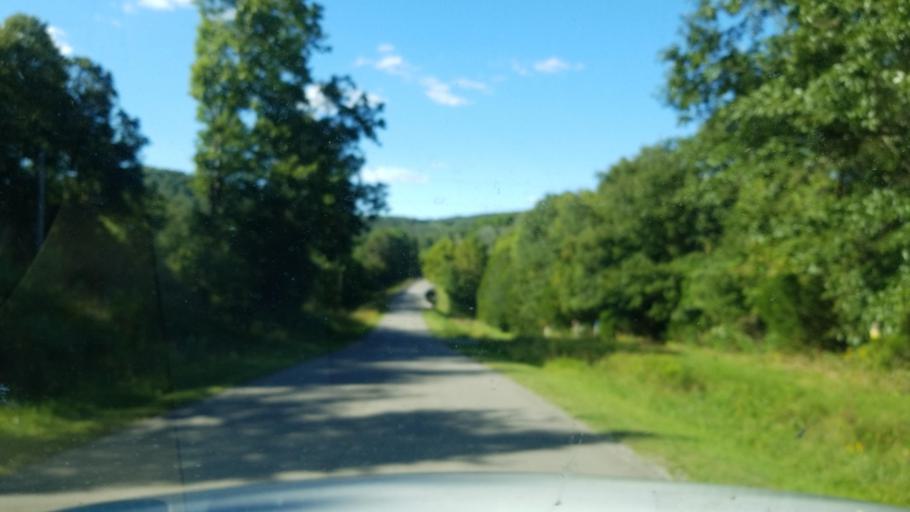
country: US
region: Illinois
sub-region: Hardin County
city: Elizabethtown
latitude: 37.5882
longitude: -88.3655
